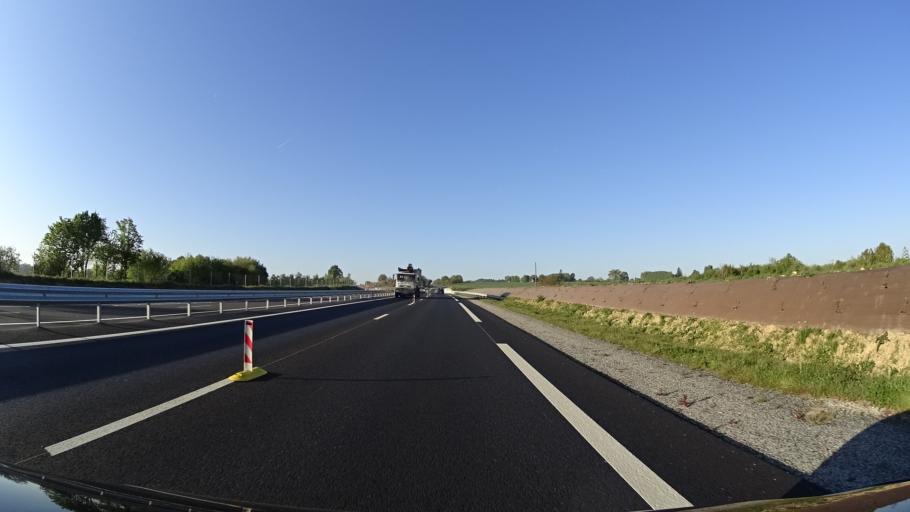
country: FR
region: Brittany
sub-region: Departement d'Ille-et-Vilaine
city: Pipriac
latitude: 47.7939
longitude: -1.9237
